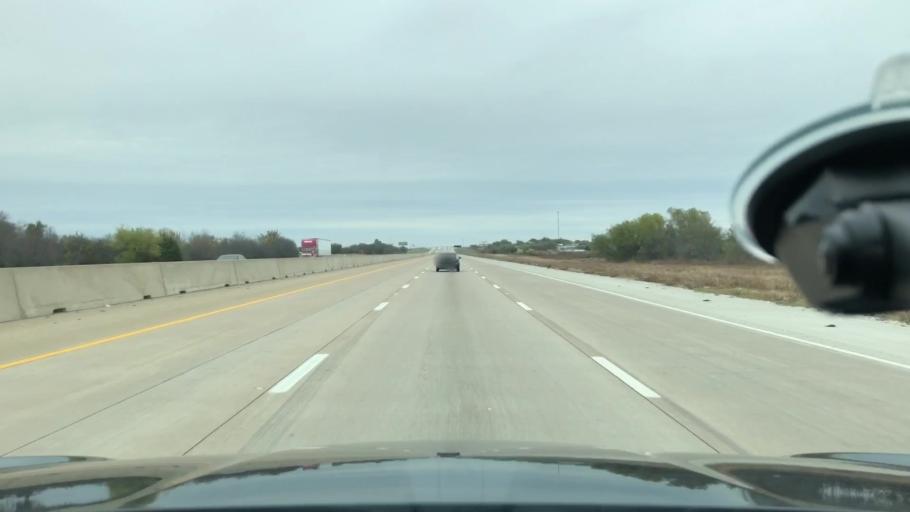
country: US
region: Texas
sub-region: Ellis County
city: Nash
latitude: 32.3035
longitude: -96.8639
